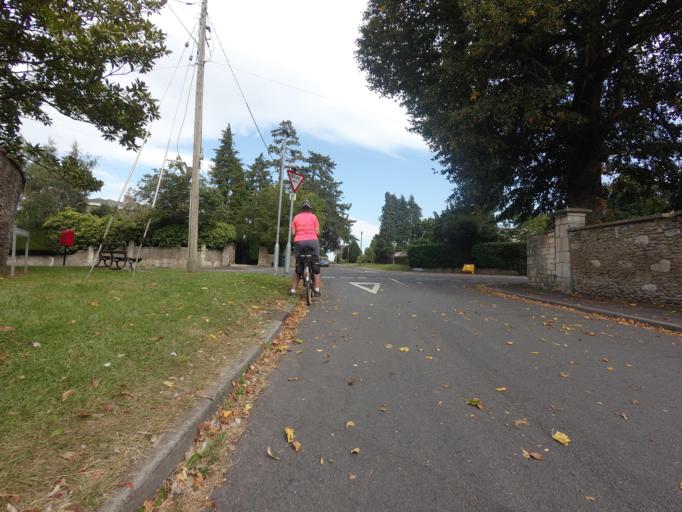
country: GB
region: England
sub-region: Wiltshire
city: Trowbridge
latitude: 51.3276
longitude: -2.1946
